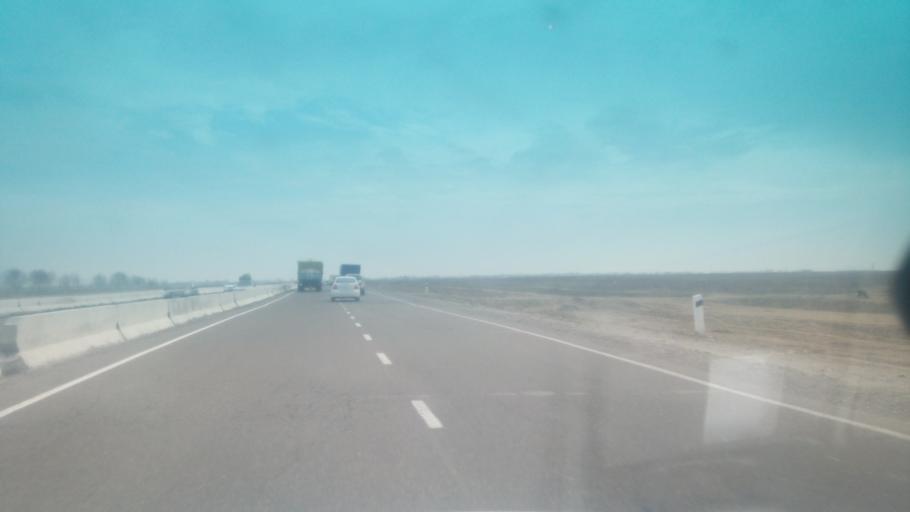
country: KZ
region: Ongtustik Qazaqstan
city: Myrzakent
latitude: 40.5137
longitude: 68.4881
